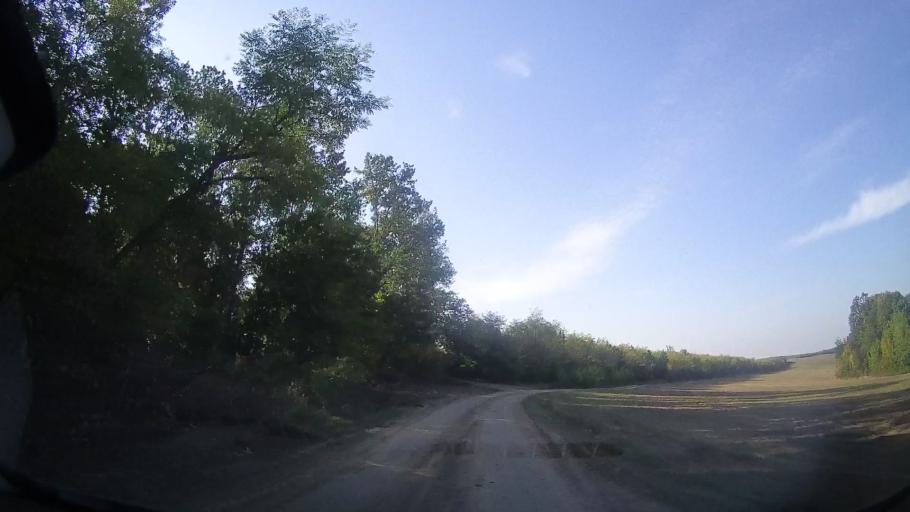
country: RO
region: Timis
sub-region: Comuna Bogda
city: Bogda
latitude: 45.9168
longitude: 21.6126
